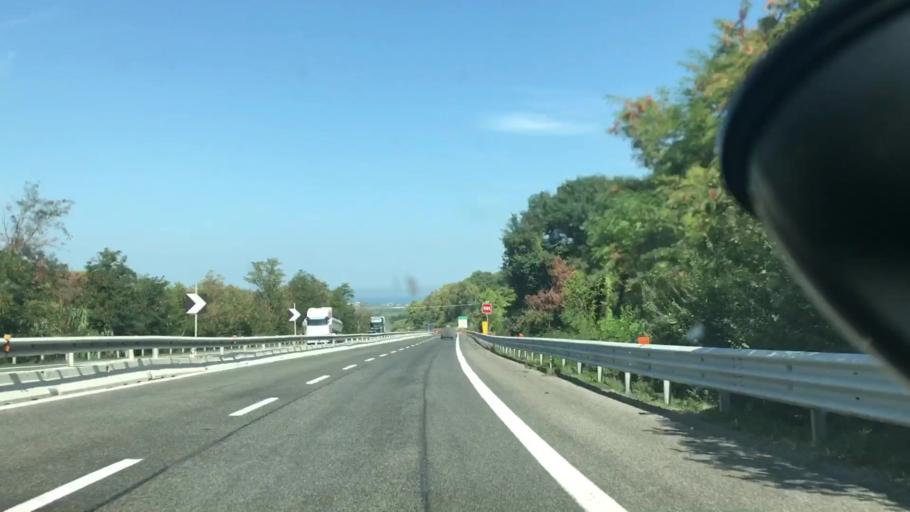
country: IT
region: Abruzzo
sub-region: Provincia di Chieti
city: Vasto
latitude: 42.1437
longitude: 14.6569
